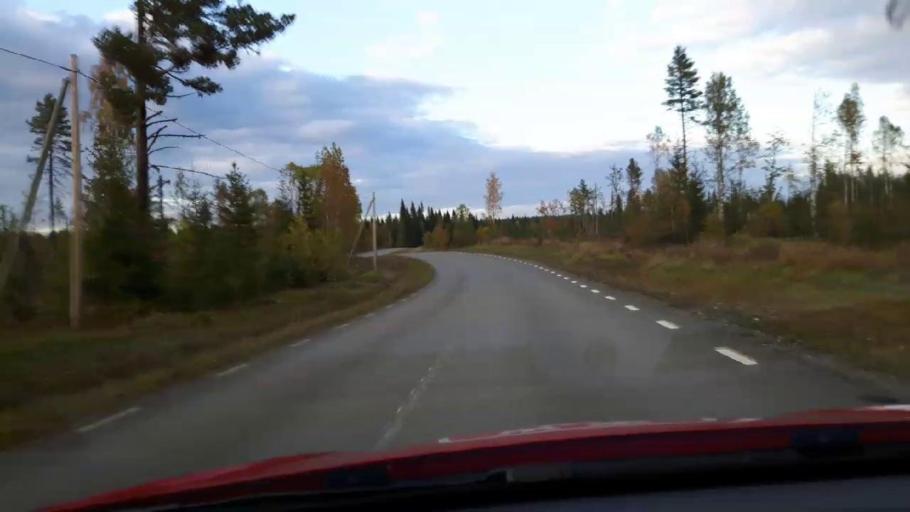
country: SE
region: Jaemtland
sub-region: OEstersunds Kommun
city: Lit
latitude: 63.3195
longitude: 15.1489
